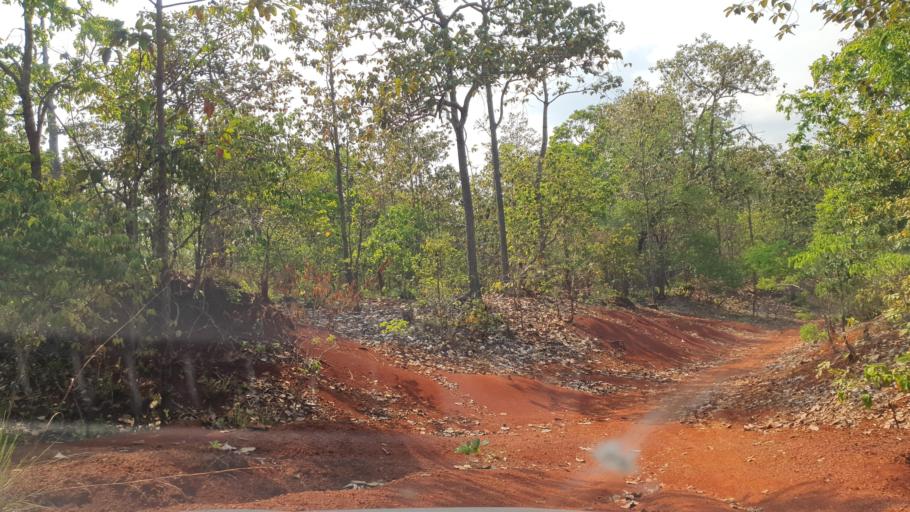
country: TH
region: Chiang Mai
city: San Sai
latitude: 19.0035
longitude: 99.1194
